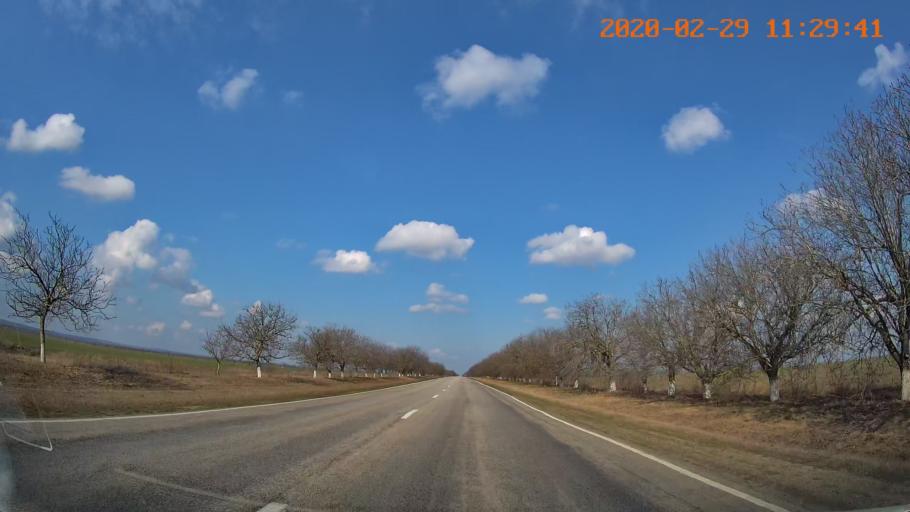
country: MD
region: Telenesti
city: Cocieri
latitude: 47.4984
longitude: 29.1232
